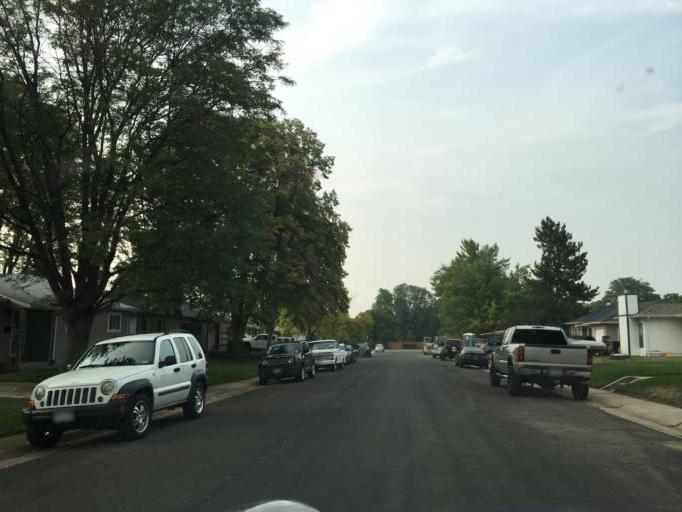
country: US
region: Colorado
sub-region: Arapahoe County
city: Glendale
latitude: 39.6841
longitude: -104.9269
